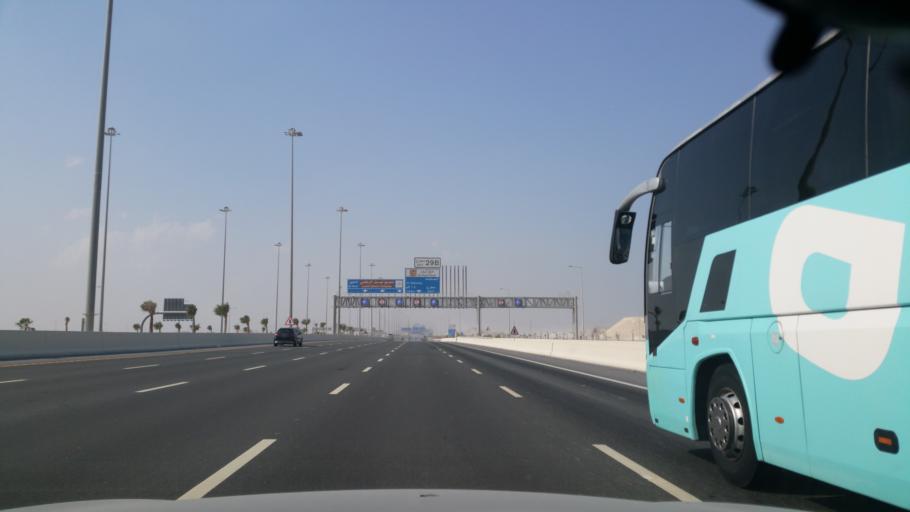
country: QA
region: Baladiyat Umm Salal
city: Umm Salal Muhammad
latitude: 25.4339
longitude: 51.4837
